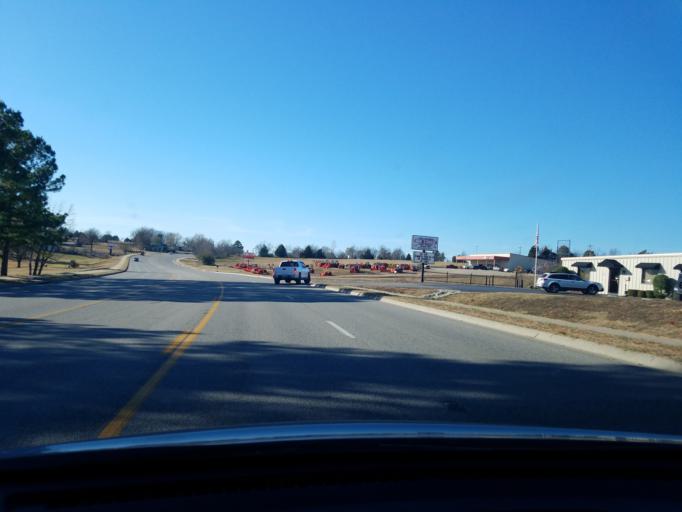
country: US
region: Arkansas
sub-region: Carroll County
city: Berryville
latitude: 36.3821
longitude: -93.5957
